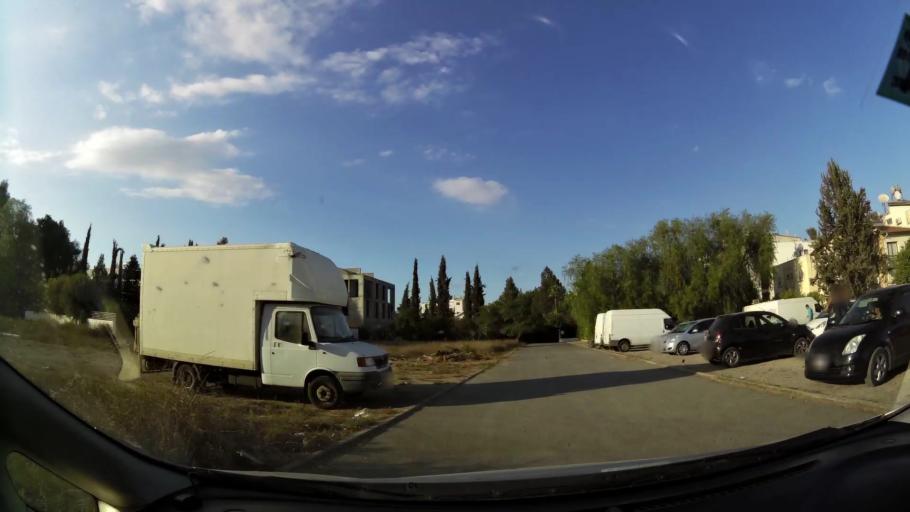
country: CY
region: Lefkosia
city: Nicosia
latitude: 35.1875
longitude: 33.3535
